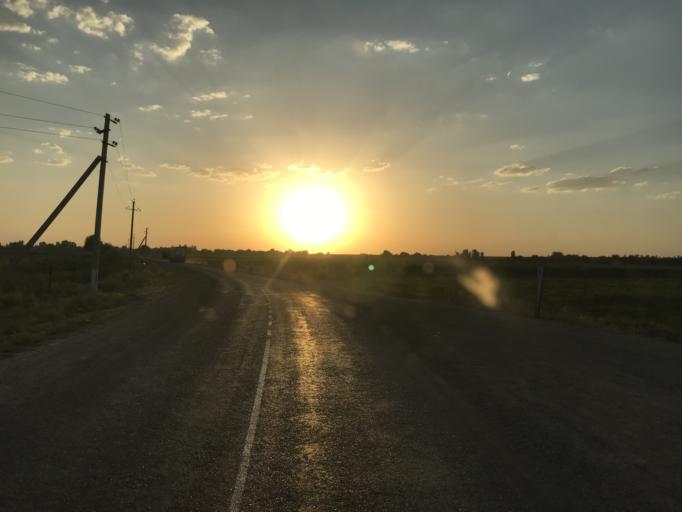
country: UZ
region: Toshkent
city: Yangiyul
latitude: 41.3754
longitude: 68.8247
